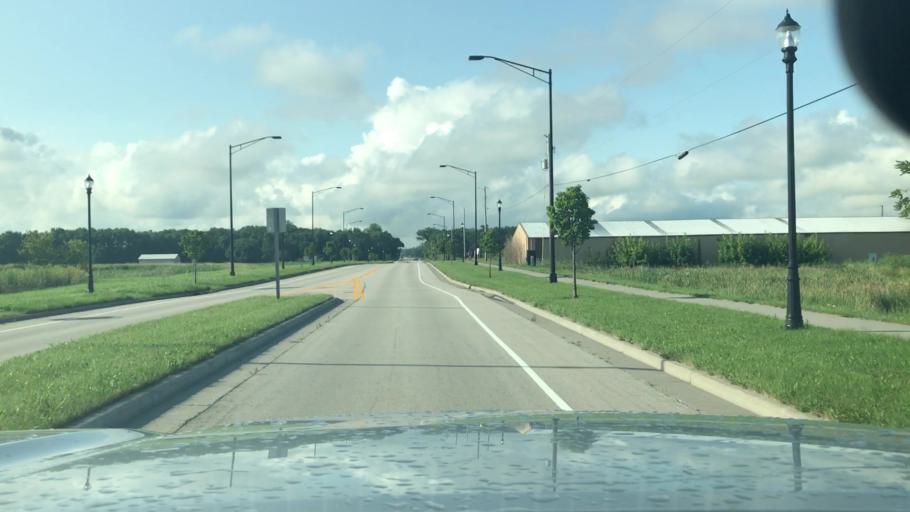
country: US
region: Wisconsin
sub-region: Brown County
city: Bellevue
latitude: 44.4635
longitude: -87.9174
